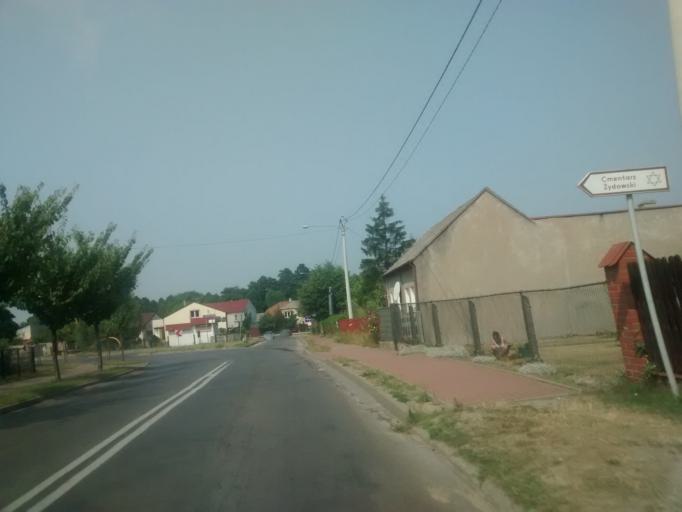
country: PL
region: Silesian Voivodeship
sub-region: Powiat myszkowski
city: Zarki
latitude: 50.6307
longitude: 19.3776
